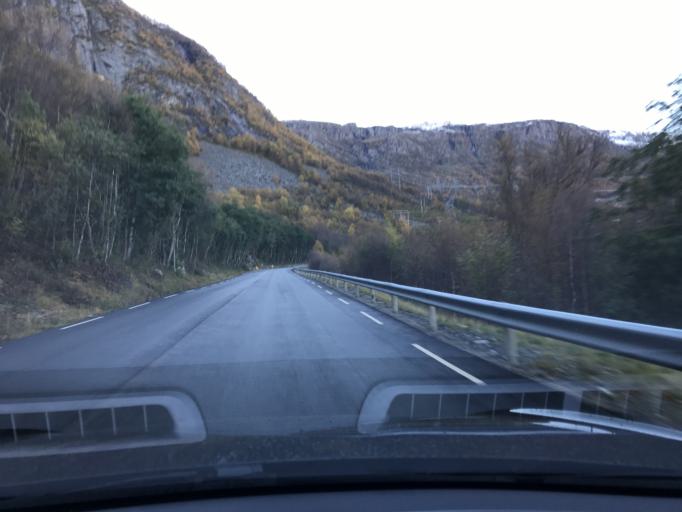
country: NO
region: Sogn og Fjordane
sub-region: Aurland
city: Aurlandsvangen
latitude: 60.8540
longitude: 7.3145
